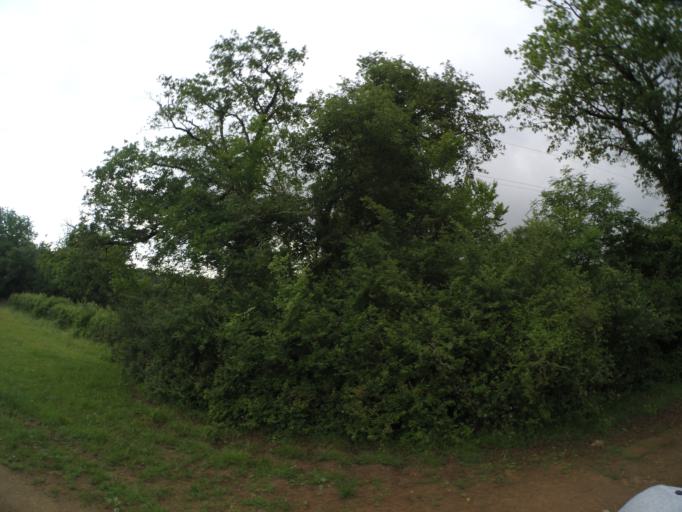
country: FR
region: Pays de la Loire
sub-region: Departement de la Vendee
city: Nesmy
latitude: 46.6035
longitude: -1.3738
